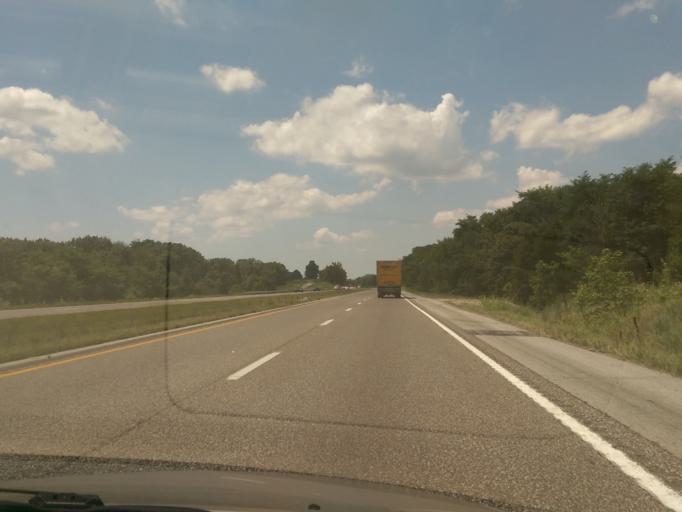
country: US
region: Missouri
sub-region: Boone County
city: Columbia
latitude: 38.9741
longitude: -92.5072
